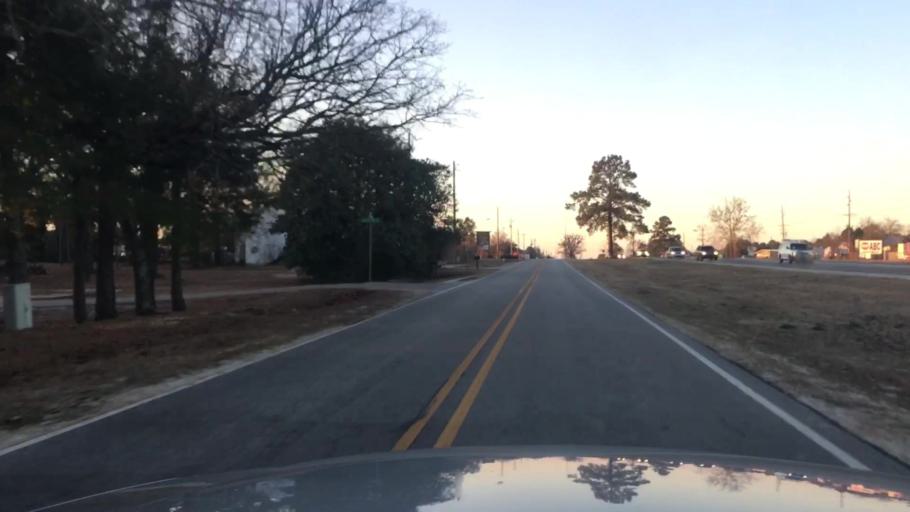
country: US
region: North Carolina
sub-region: Cumberland County
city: Hope Mills
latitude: 34.9857
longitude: -78.9043
